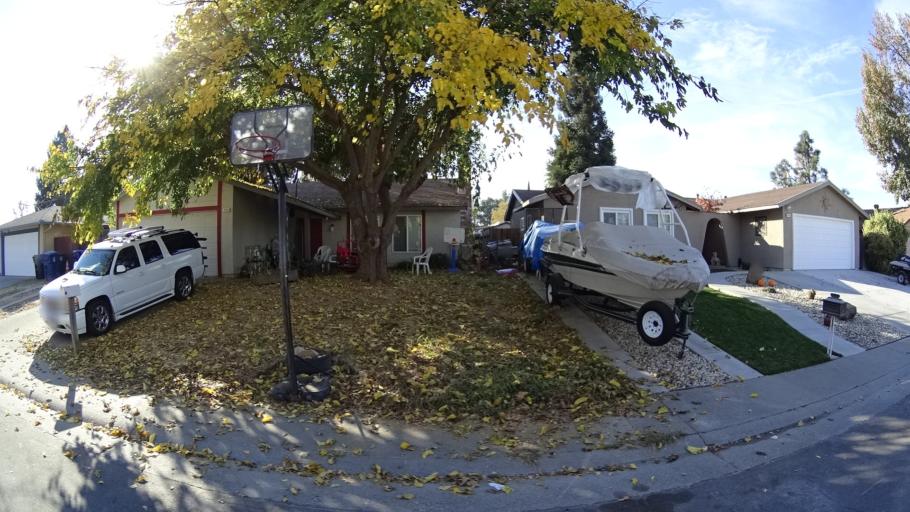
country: US
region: California
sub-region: Sacramento County
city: Antelope
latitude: 38.7033
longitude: -121.3216
